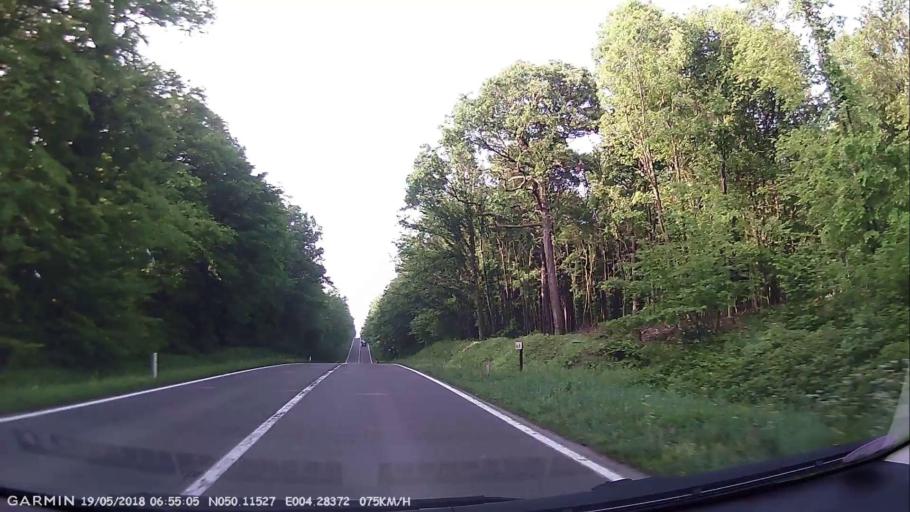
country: BE
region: Wallonia
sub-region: Province du Hainaut
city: Froidchapelle
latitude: 50.1152
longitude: 4.2838
